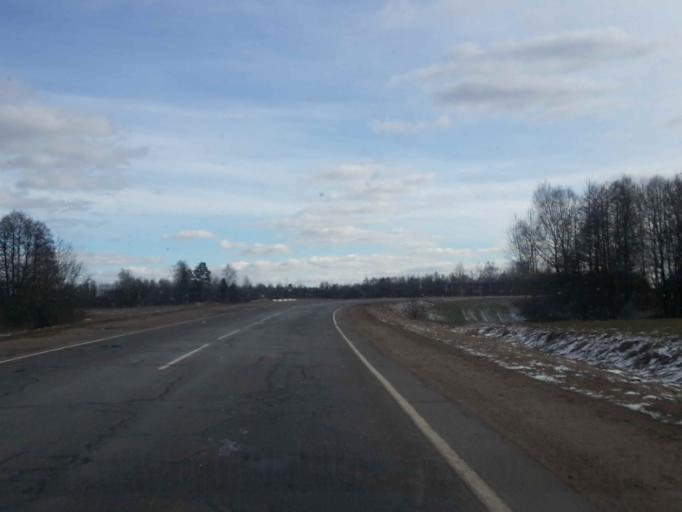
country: BY
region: Minsk
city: Myadzyel
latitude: 54.9639
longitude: 26.9004
